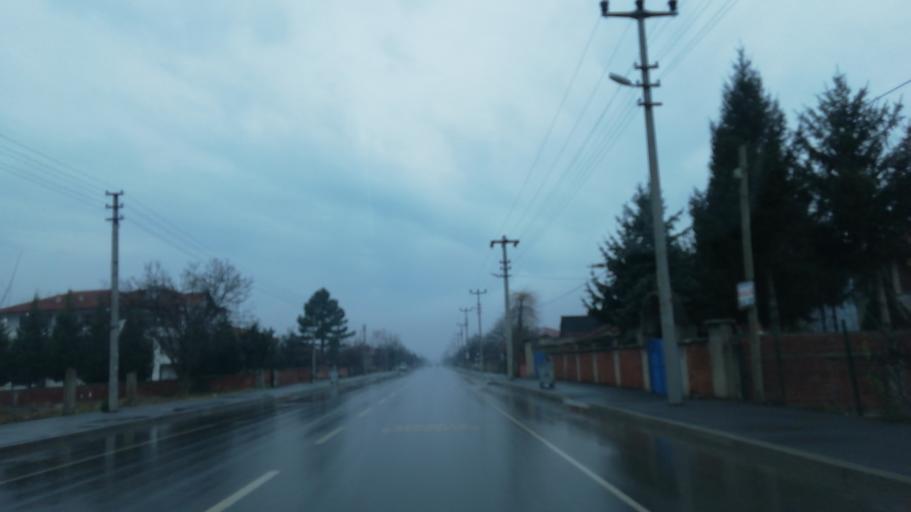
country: TR
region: Sakarya
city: Akyazi
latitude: 40.6384
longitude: 30.6257
